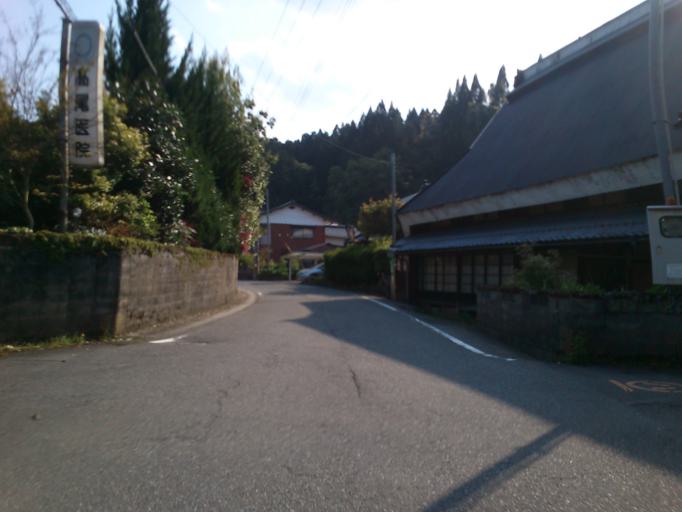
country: JP
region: Kyoto
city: Fukuchiyama
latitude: 35.3225
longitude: 135.0059
